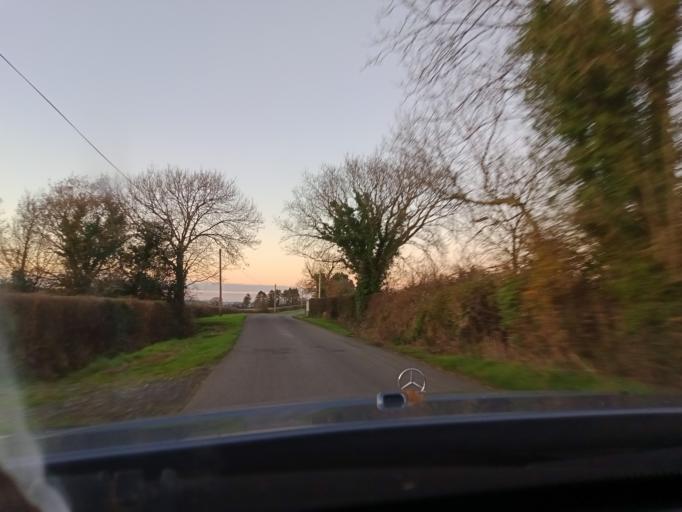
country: IE
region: Leinster
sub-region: Kilkenny
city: Thomastown
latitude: 52.4740
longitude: -7.0993
